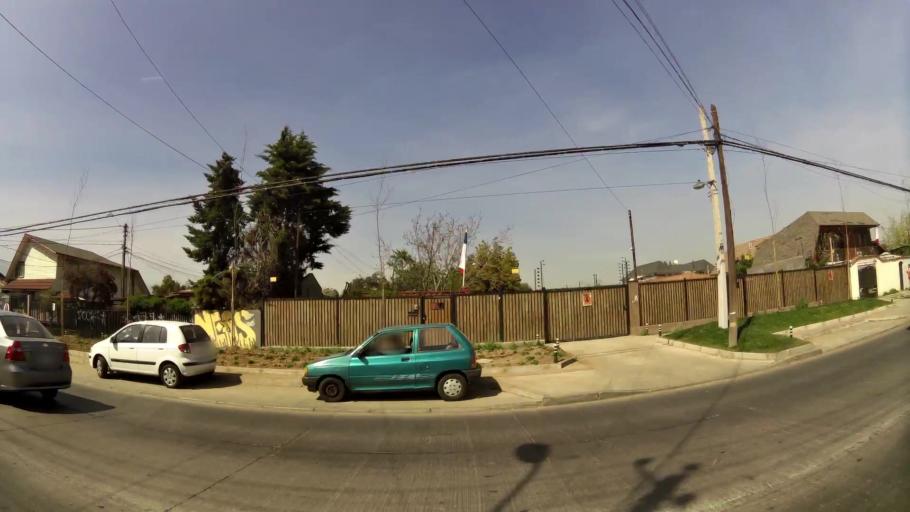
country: CL
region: Santiago Metropolitan
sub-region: Provincia de Santiago
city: Villa Presidente Frei, Nunoa, Santiago, Chile
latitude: -33.5227
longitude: -70.5858
